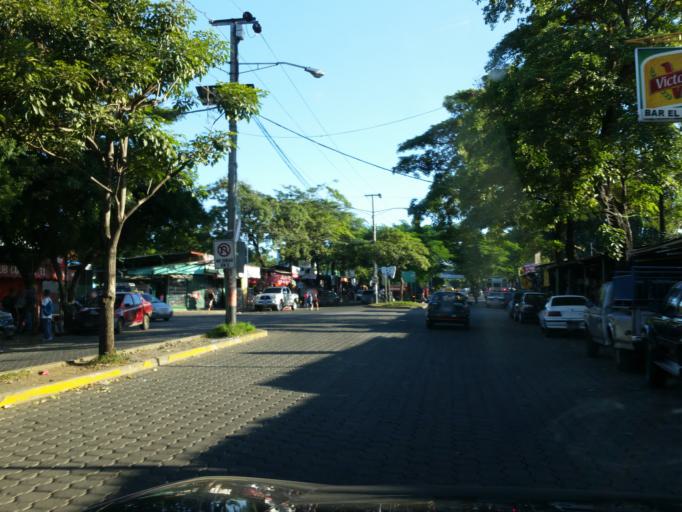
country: NI
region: Managua
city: Managua
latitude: 12.1279
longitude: -86.3014
